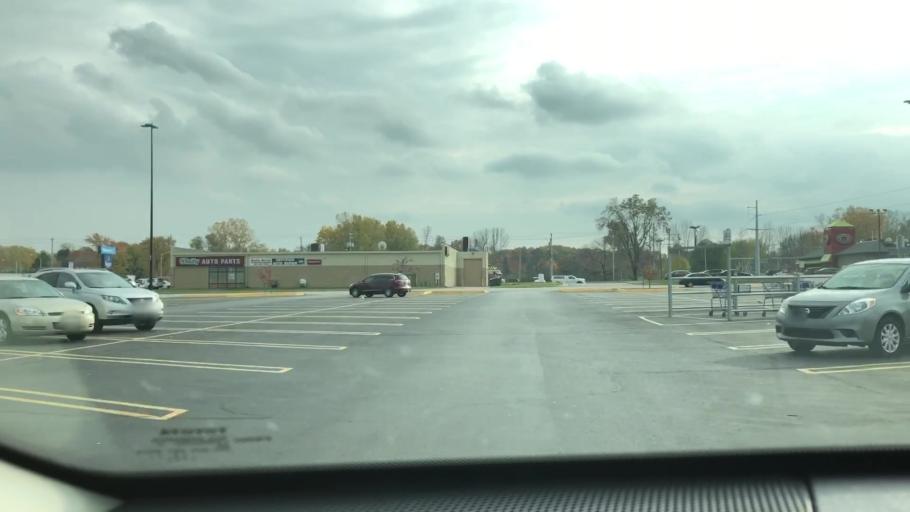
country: US
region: Wisconsin
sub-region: Brown County
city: Howard
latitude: 44.5257
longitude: -88.0933
